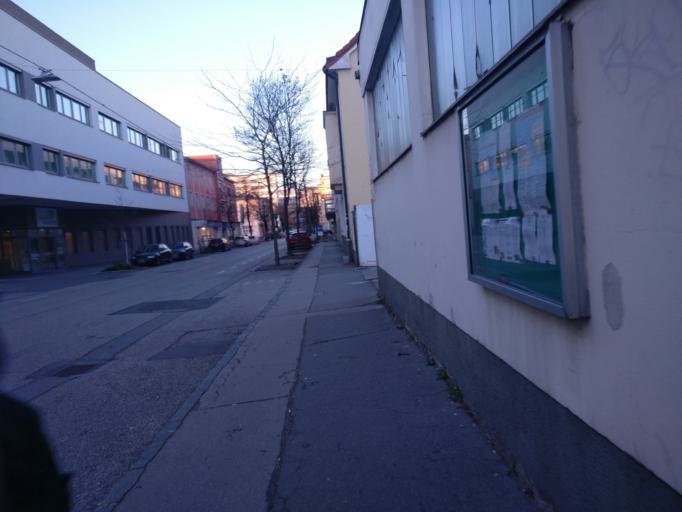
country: AT
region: Lower Austria
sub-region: Sankt Polten Stadt
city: Sankt Poelten
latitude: 48.2108
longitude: 15.6250
